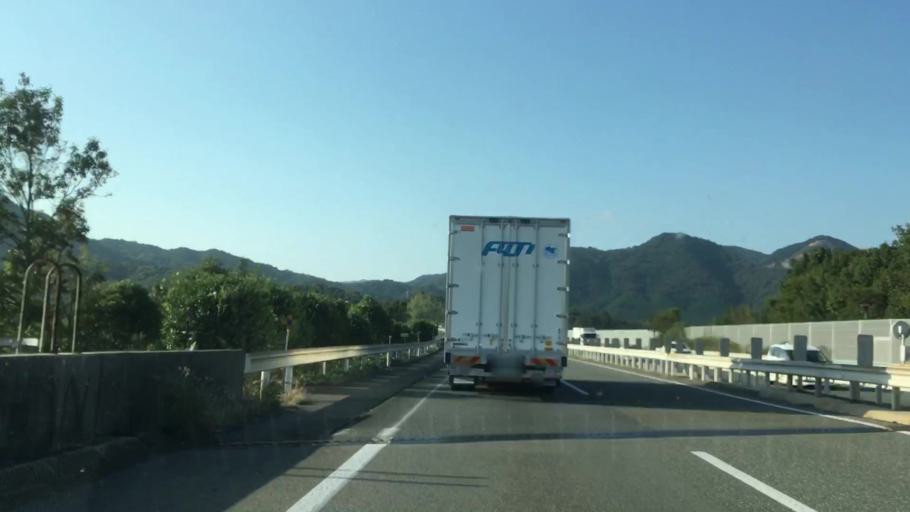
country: JP
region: Yamaguchi
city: Hofu
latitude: 34.0700
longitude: 131.4982
